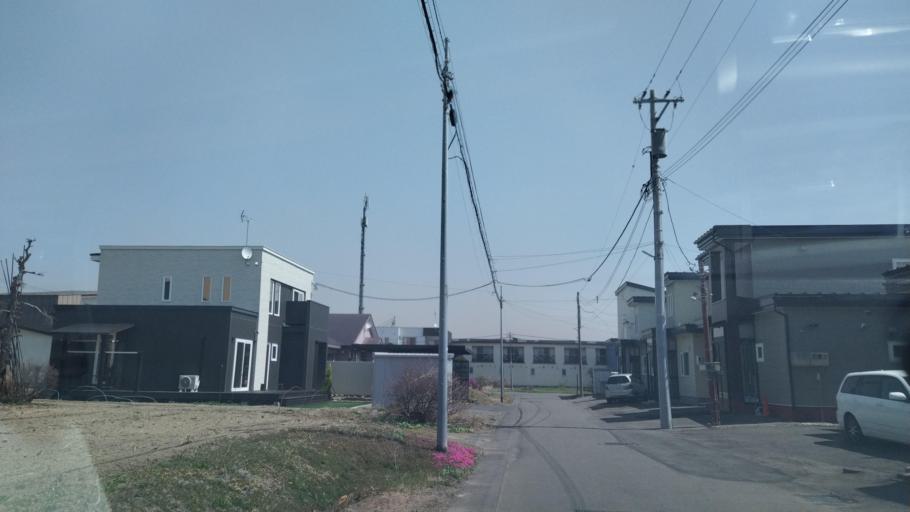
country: JP
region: Hokkaido
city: Obihiro
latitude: 42.9403
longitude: 143.1867
